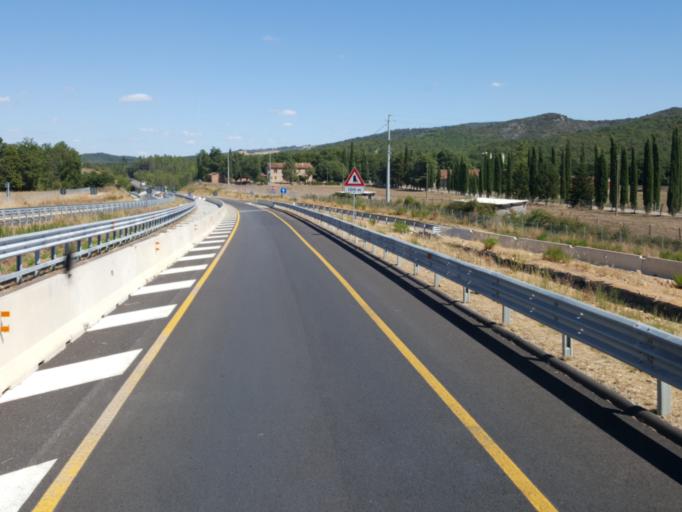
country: IT
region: Tuscany
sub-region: Provincia di Siena
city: Murlo
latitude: 43.1159
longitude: 11.2969
